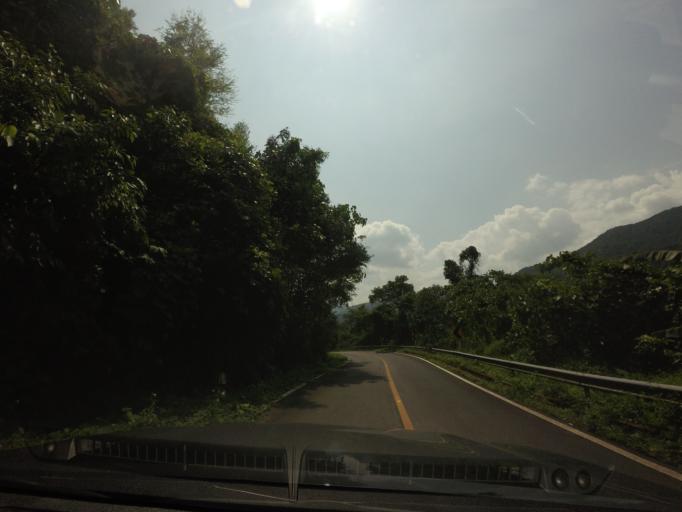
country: TH
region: Nan
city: Bo Kluea
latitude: 19.1582
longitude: 101.1598
